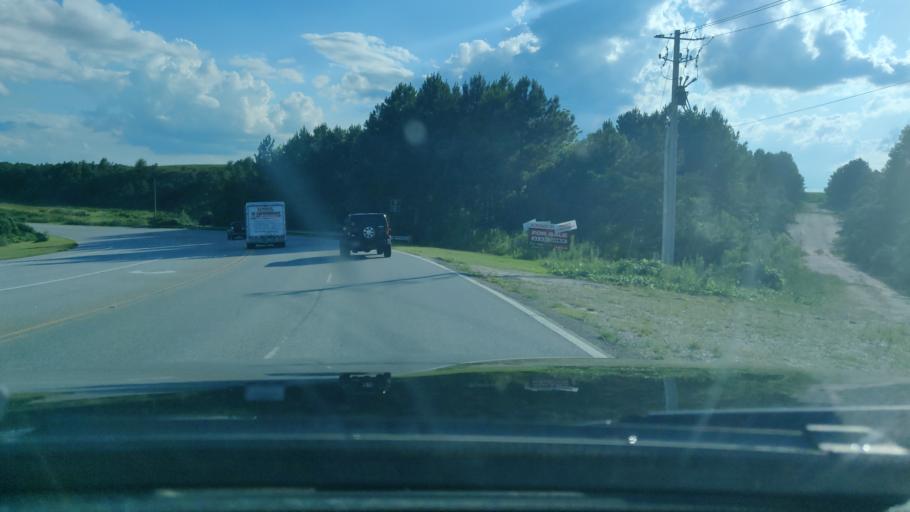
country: US
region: Alabama
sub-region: Lee County
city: Auburn
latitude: 32.6088
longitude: -85.4315
